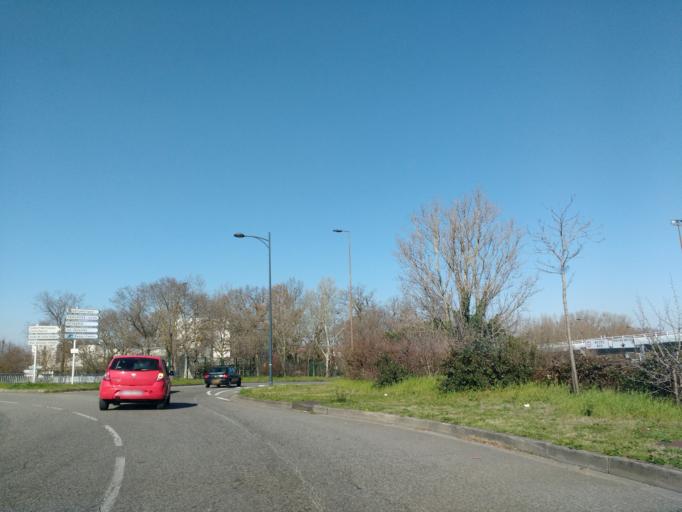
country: FR
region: Midi-Pyrenees
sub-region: Departement de la Haute-Garonne
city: Portet-sur-Garonne
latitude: 43.5701
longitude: 1.3911
